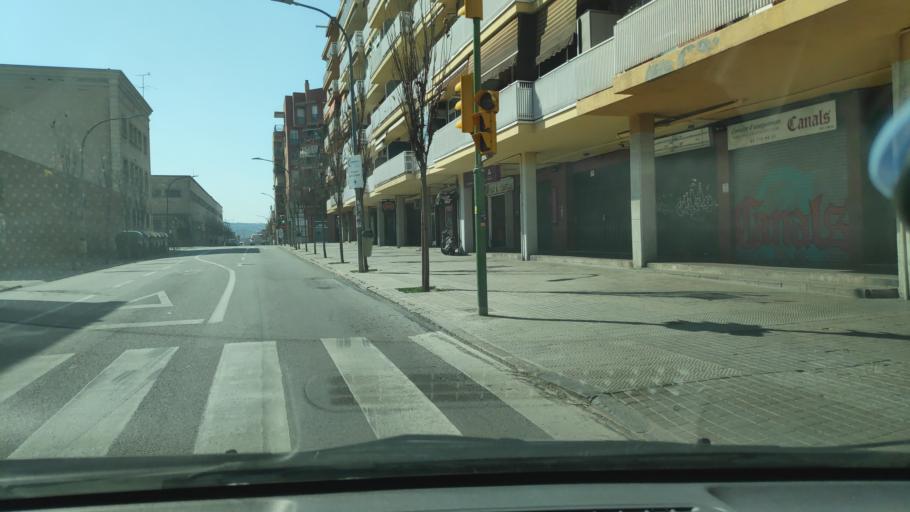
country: ES
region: Catalonia
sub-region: Provincia de Barcelona
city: Sabadell
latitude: 41.5351
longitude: 2.1157
